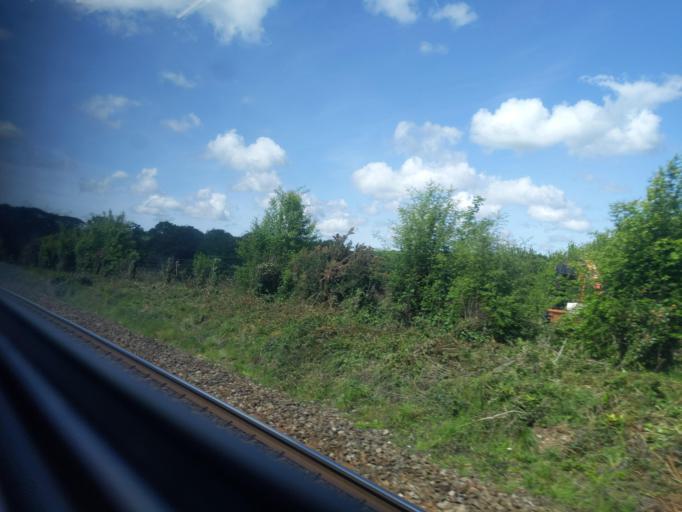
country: GB
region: England
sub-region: Cornwall
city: Liskeard
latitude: 50.4547
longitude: -4.4997
